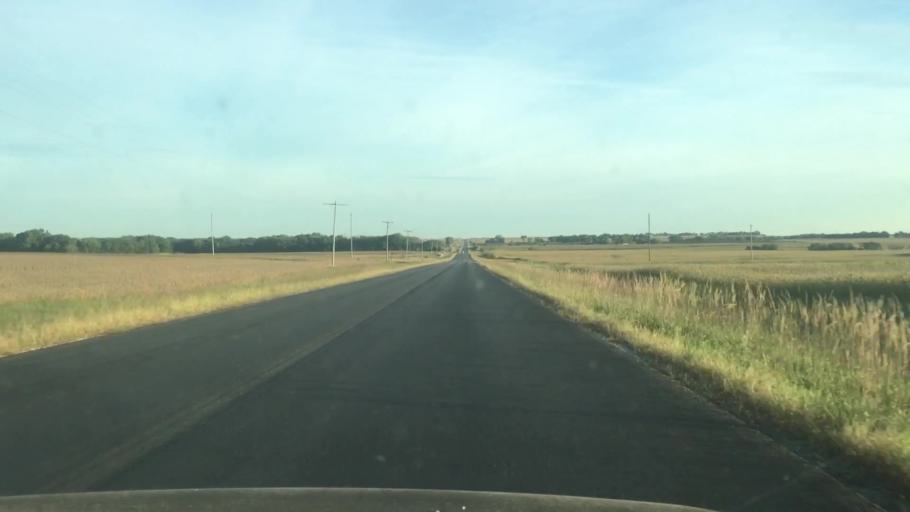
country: US
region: Kansas
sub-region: Marshall County
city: Marysville
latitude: 39.8691
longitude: -96.6004
